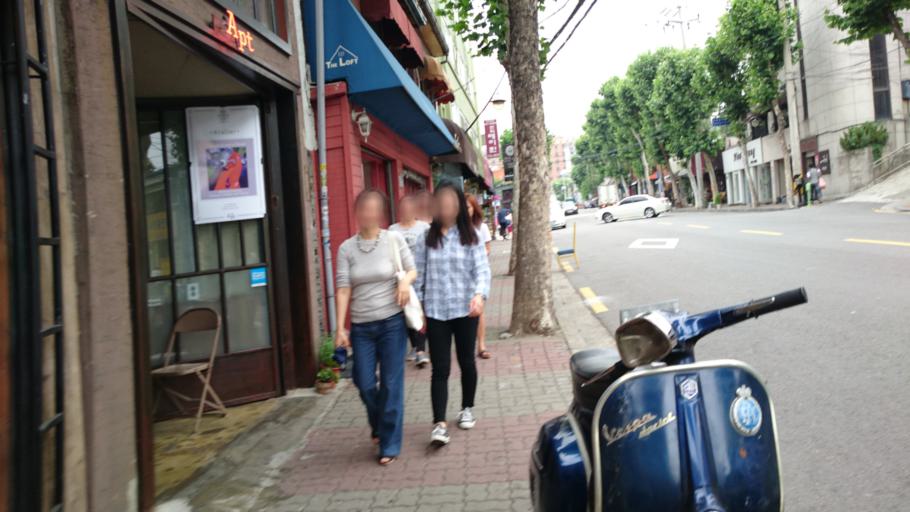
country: KR
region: Seoul
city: Seoul
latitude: 37.5318
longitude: 126.9948
